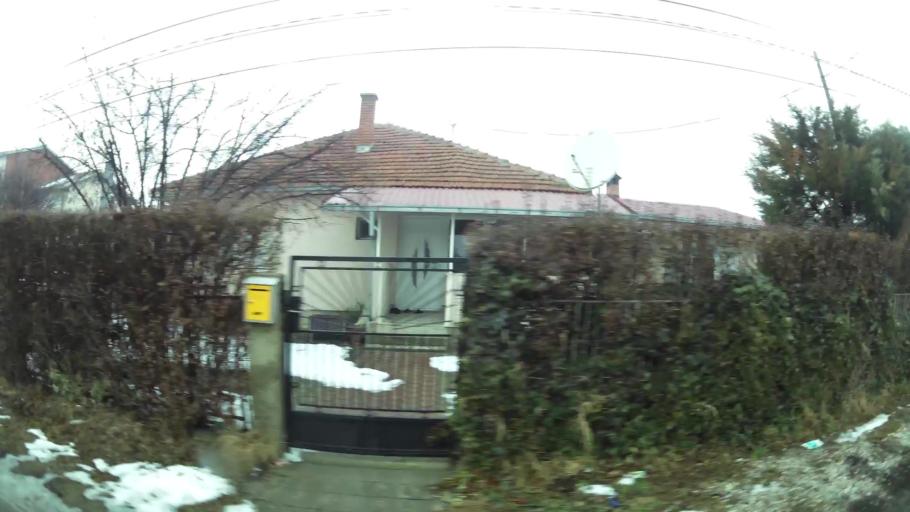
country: MK
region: Petrovec
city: Petrovec
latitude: 41.9371
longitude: 21.6162
